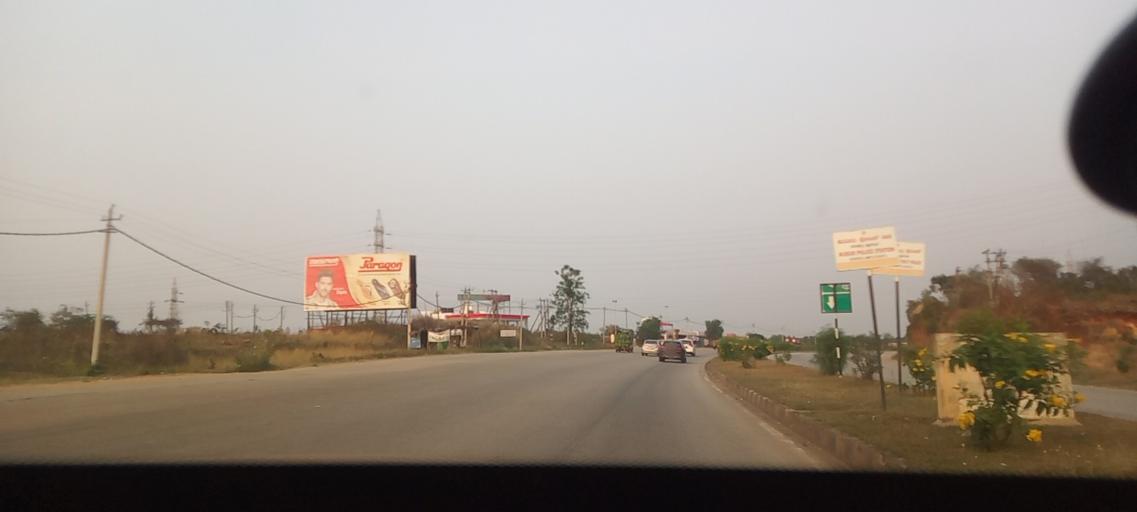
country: IN
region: Karnataka
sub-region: Tumkur
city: Kunigal
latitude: 13.0340
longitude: 77.0853
